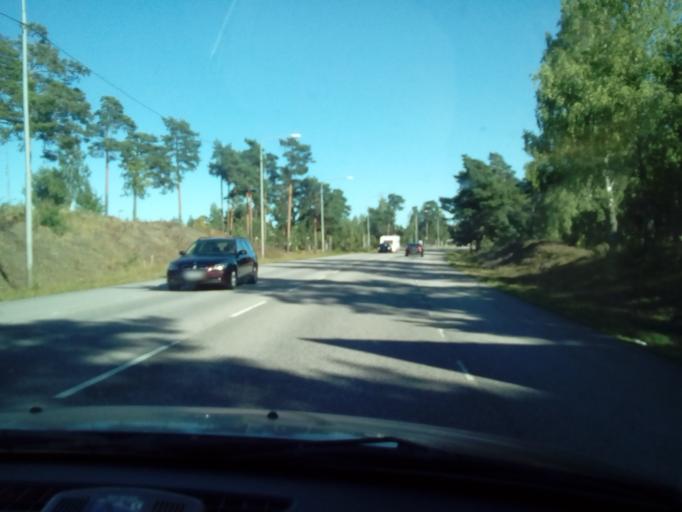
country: SE
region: Kalmar
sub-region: Vasterviks Kommun
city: Vaestervik
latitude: 57.7667
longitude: 16.5959
